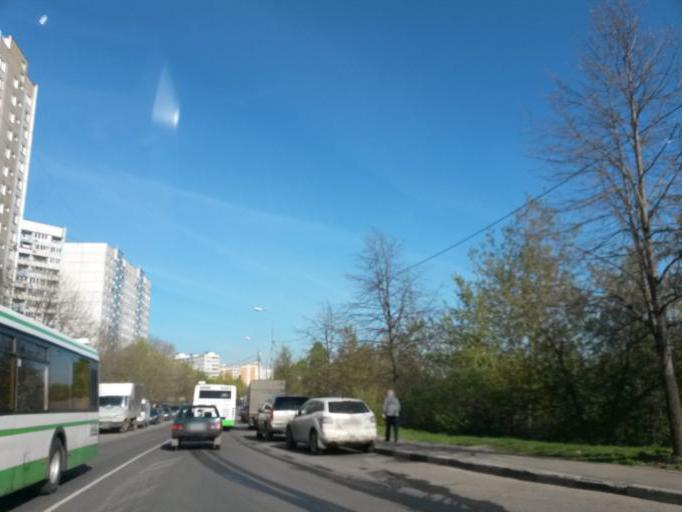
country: RU
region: Moscow
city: Zyablikovo
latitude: 55.6209
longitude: 37.7610
